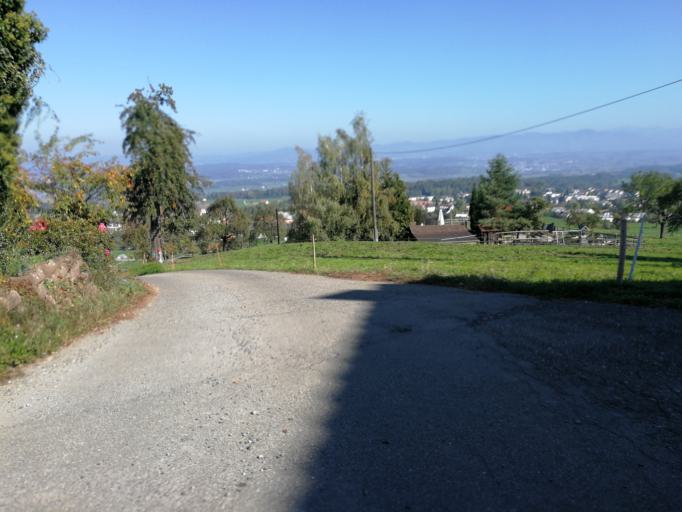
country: CH
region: Zurich
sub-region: Bezirk Uster
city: Hinteregg
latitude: 47.3029
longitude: 8.6762
